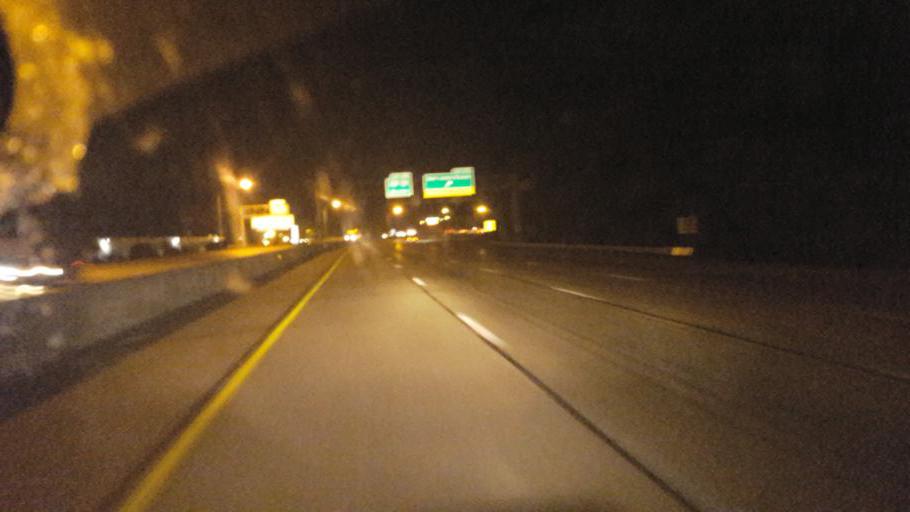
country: US
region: Indiana
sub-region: Marion County
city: Speedway
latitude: 39.7372
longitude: -86.2389
